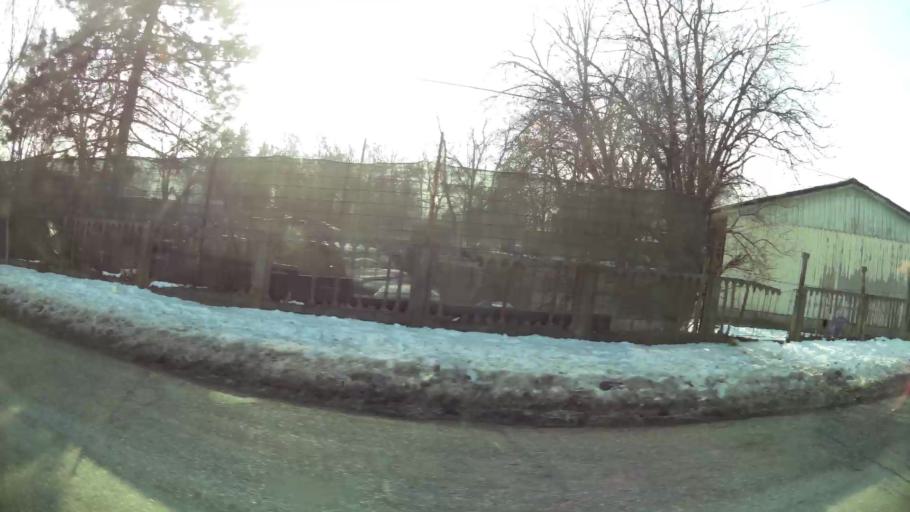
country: MK
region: Suto Orizari
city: Suto Orizare
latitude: 42.0162
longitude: 21.3911
